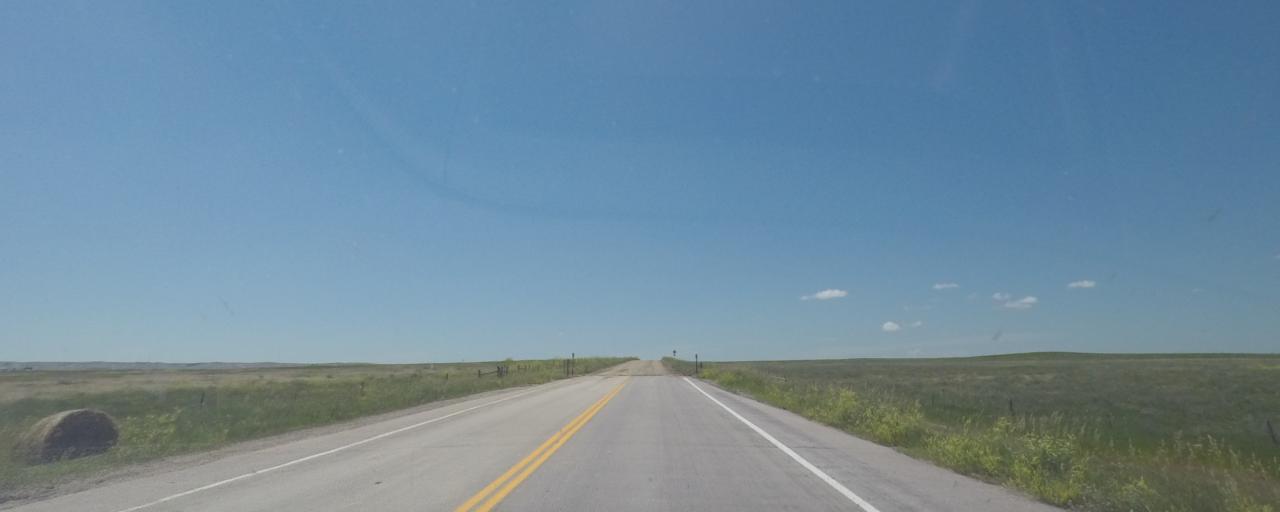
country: US
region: South Dakota
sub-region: Haakon County
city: Philip
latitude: 43.9367
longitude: -102.1539
